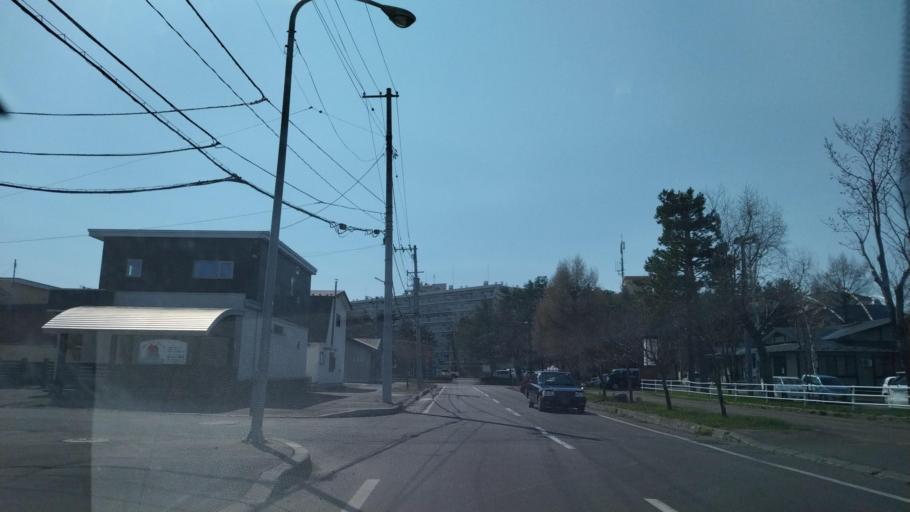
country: JP
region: Hokkaido
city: Obihiro
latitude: 42.9081
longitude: 143.1987
